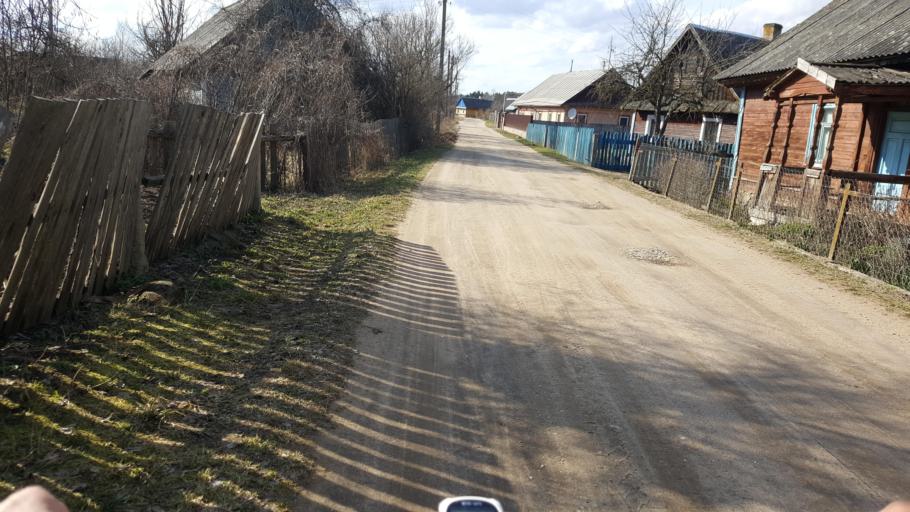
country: BY
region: Brest
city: Kamyanyets
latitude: 52.4168
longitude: 23.9238
